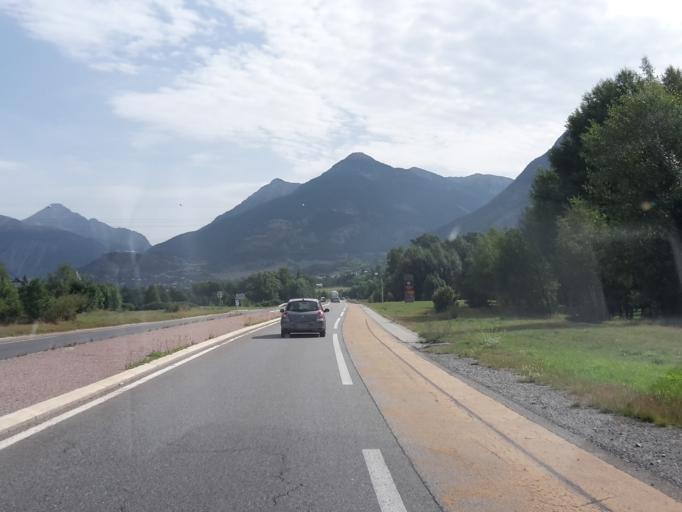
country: FR
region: Provence-Alpes-Cote d'Azur
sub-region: Departement des Hautes-Alpes
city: Villar-Saint-Pancrace
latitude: 44.8716
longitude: 6.6078
